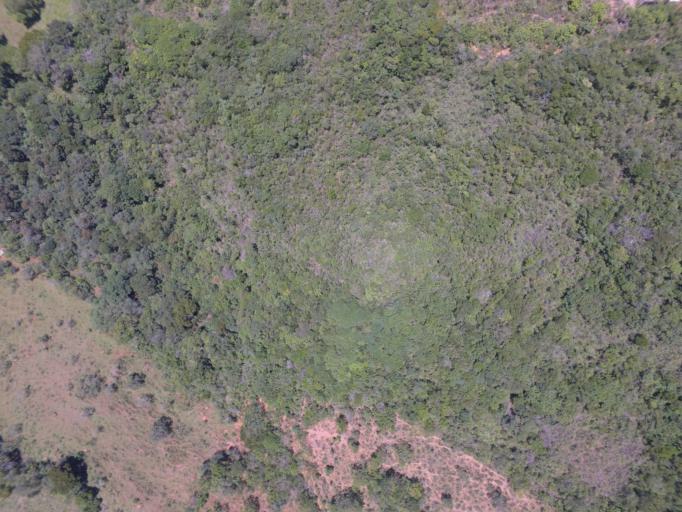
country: BR
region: Minas Gerais
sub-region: Tiradentes
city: Tiradentes
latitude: -21.0663
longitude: -44.0798
